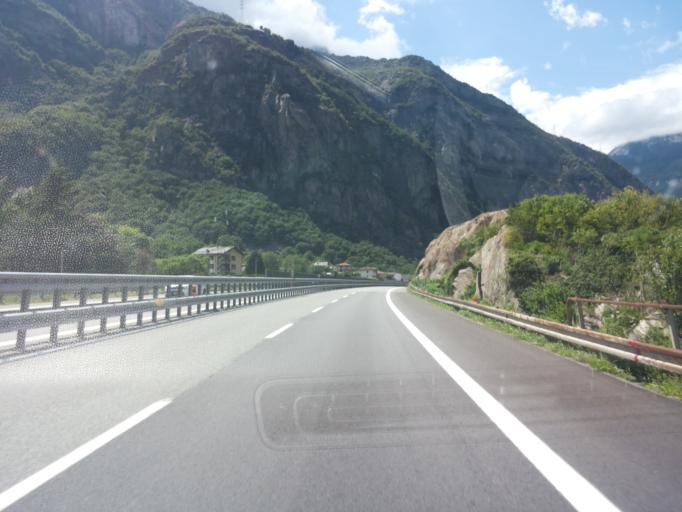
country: IT
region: Aosta Valley
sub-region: Valle d'Aosta
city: Donnas
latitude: 45.6012
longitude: 7.7632
